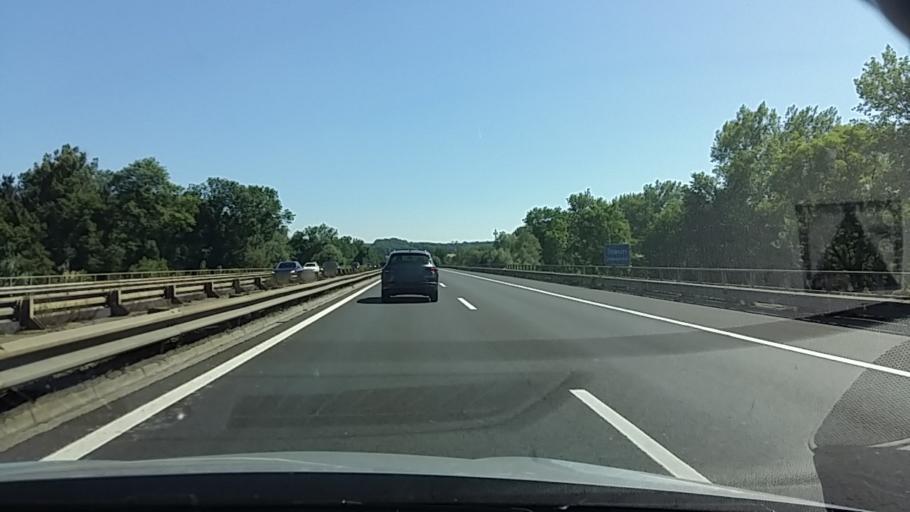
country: AT
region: Upper Austria
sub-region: Politischer Bezirk Linz-Land
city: Ansfelden
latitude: 48.2364
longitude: 14.2976
